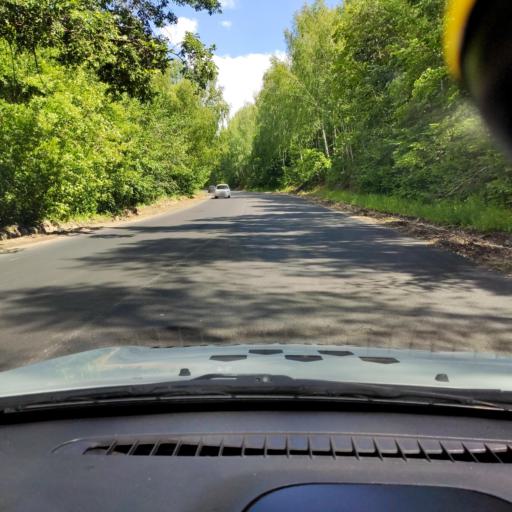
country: RU
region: Samara
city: Zhigulevsk
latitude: 53.3925
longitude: 49.4249
